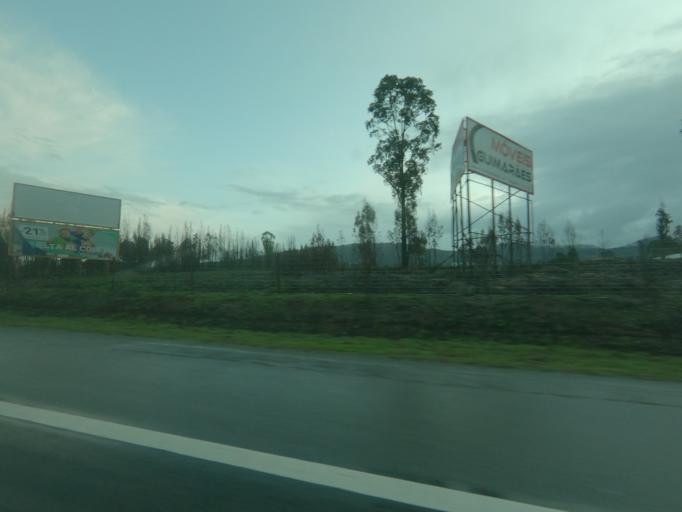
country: PT
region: Viana do Castelo
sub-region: Valenca
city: Valenza
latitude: 41.9986
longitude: -8.6431
